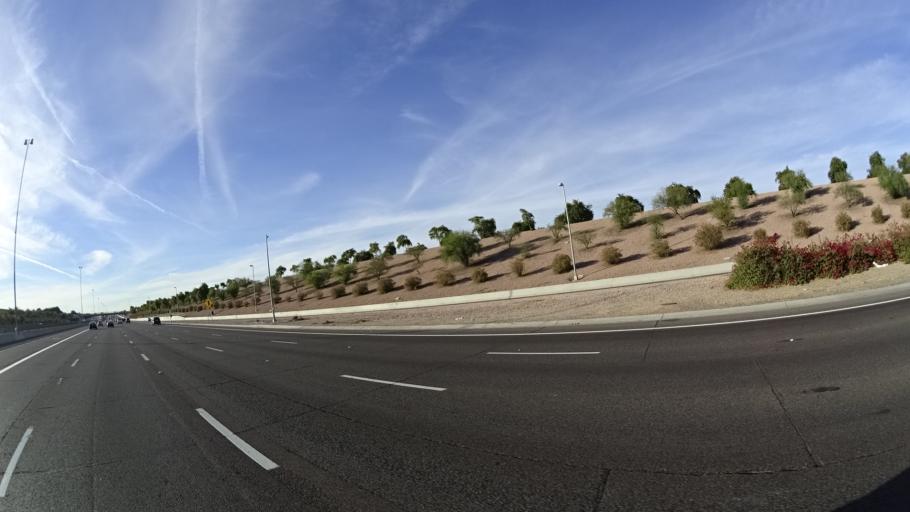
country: US
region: Arizona
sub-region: Maricopa County
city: Gilbert
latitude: 33.3866
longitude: -111.7562
